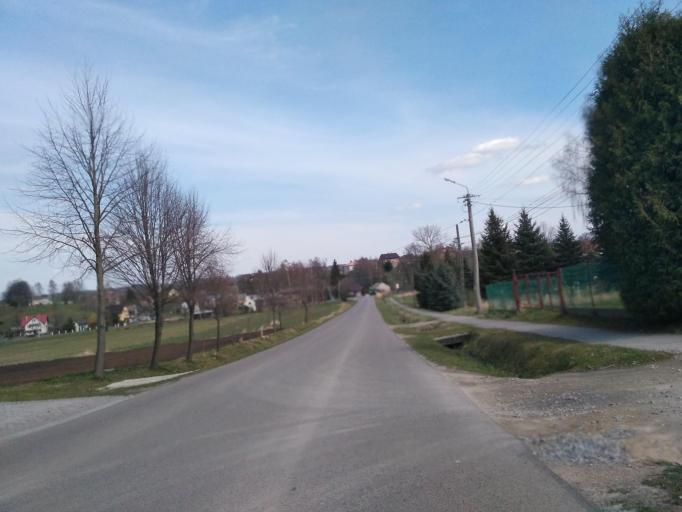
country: PL
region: Subcarpathian Voivodeship
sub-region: Powiat ropczycko-sedziszowski
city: Iwierzyce
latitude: 50.0185
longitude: 21.7859
